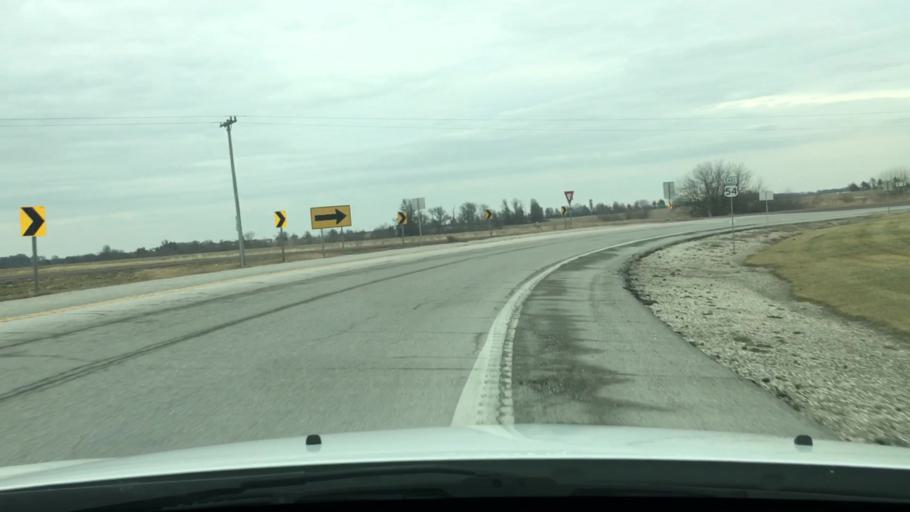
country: US
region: Missouri
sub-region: Audrain County
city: Vandalia
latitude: 39.2805
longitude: -91.6439
